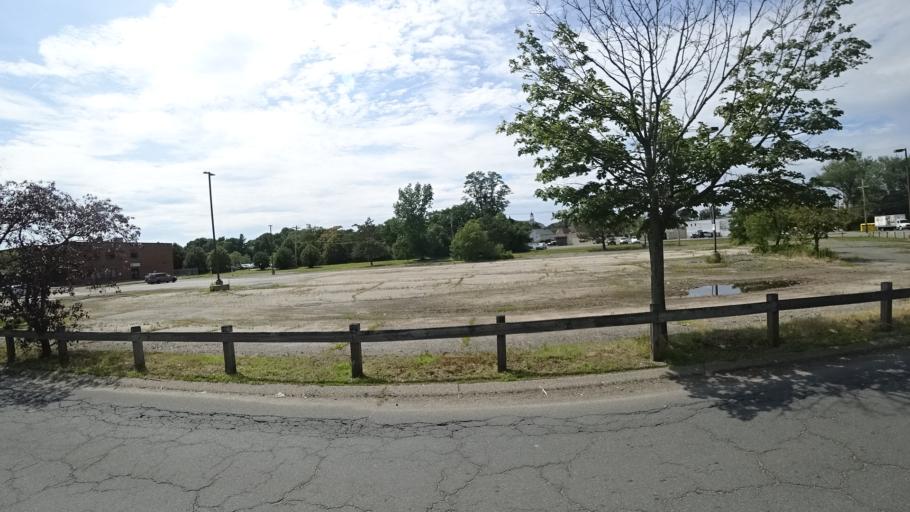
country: US
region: Massachusetts
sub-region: Norfolk County
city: Dedham
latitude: 42.2442
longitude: -71.1712
